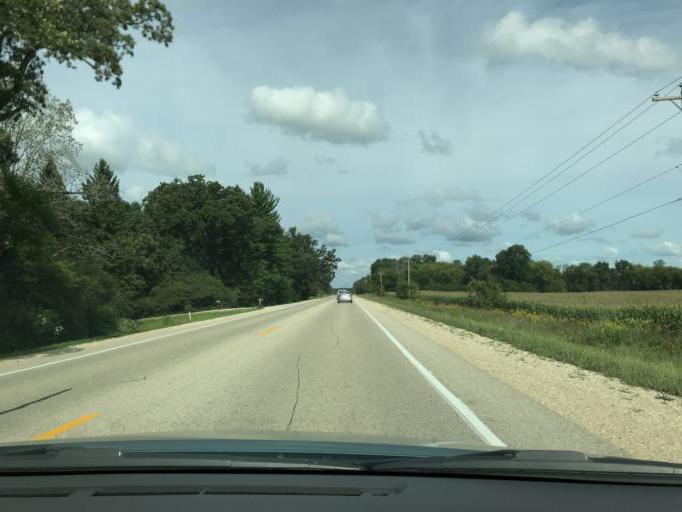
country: US
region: Wisconsin
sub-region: Racine County
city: Bohners Lake
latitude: 42.6190
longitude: -88.2367
